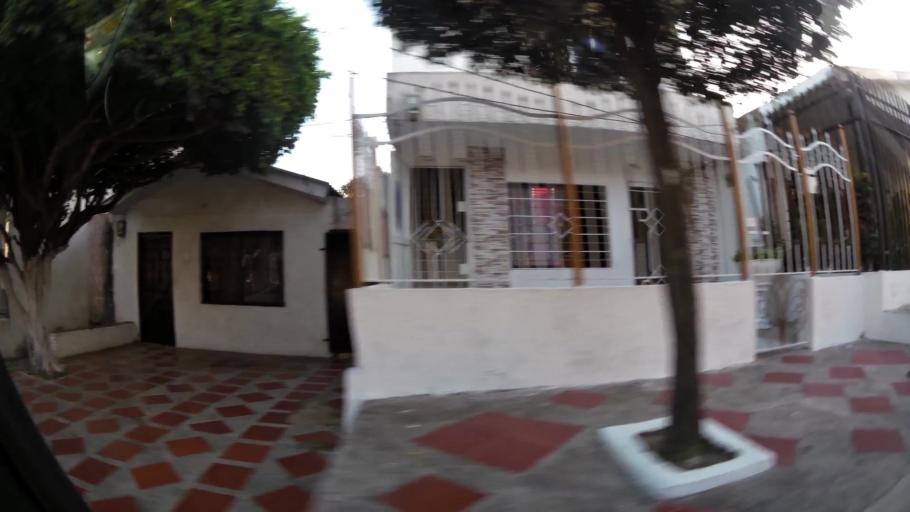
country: CO
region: Atlantico
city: Barranquilla
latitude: 10.9729
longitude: -74.8116
